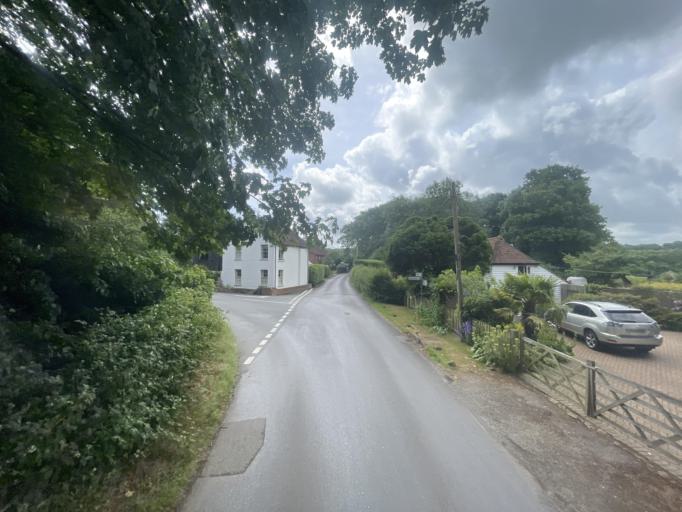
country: GB
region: England
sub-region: Kent
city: Edenbridge
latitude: 51.1574
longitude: 0.1506
